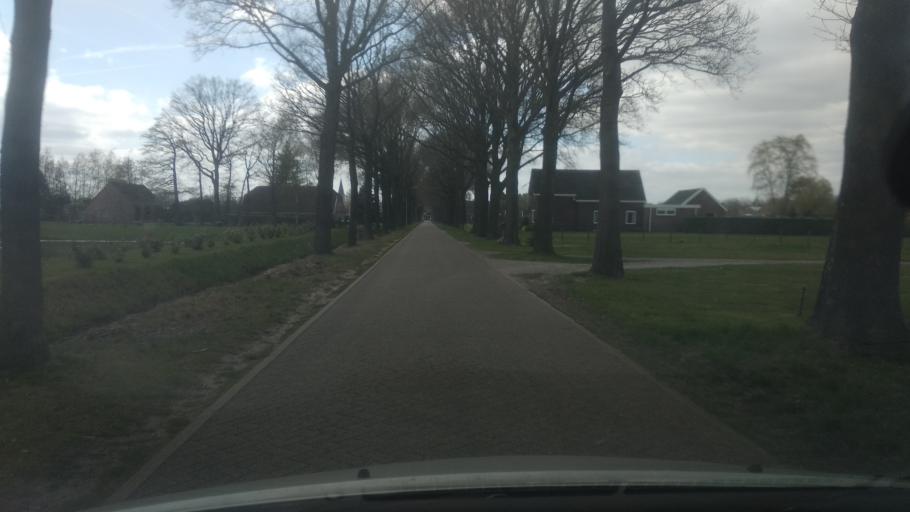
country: NL
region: Drenthe
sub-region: Gemeente Emmen
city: Emmer-Compascuum
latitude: 52.9177
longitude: 7.0344
